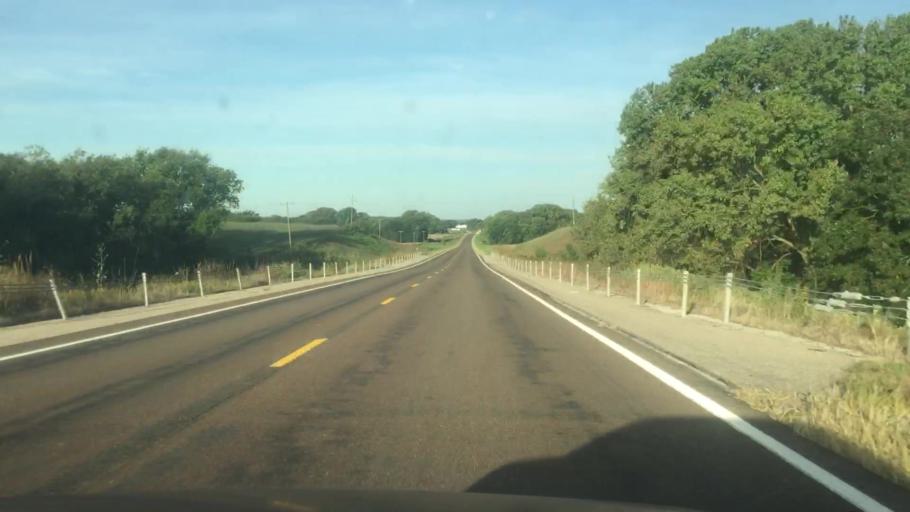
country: US
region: Nebraska
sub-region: Gage County
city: Wymore
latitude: 40.0455
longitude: -96.7730
